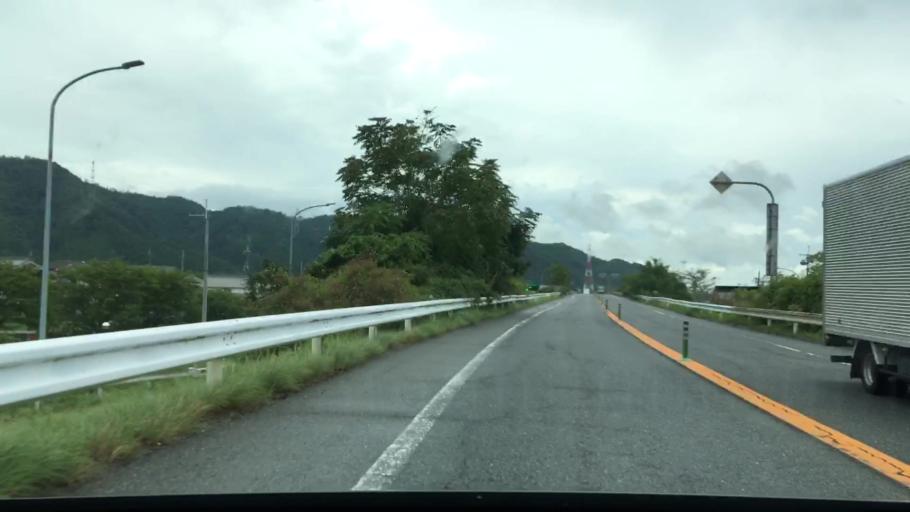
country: JP
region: Hyogo
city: Himeji
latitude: 34.9856
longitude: 134.7702
